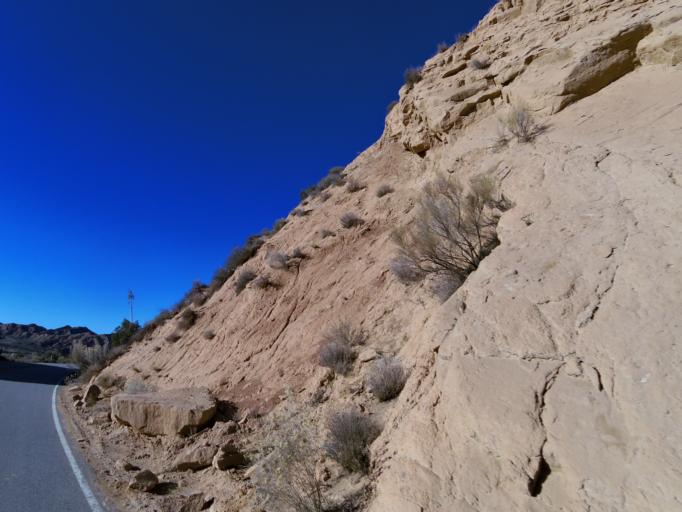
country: US
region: California
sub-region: Kern County
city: Maricopa
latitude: 34.7795
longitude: -119.4312
